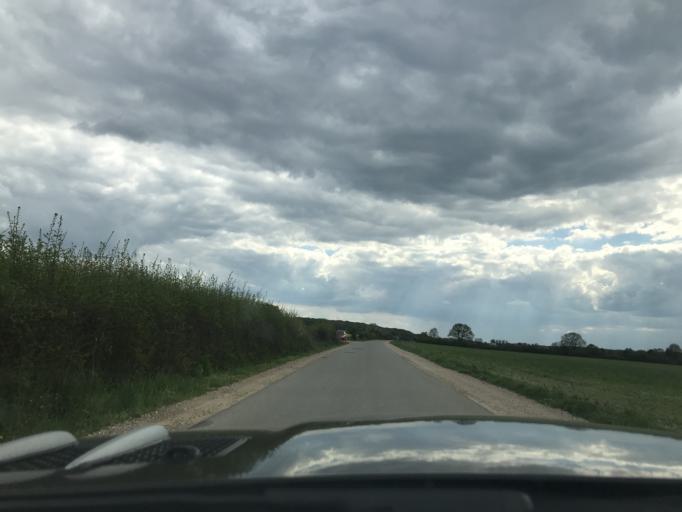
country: DE
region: Schleswig-Holstein
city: Gross Gronau
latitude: 53.7777
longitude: 10.7799
